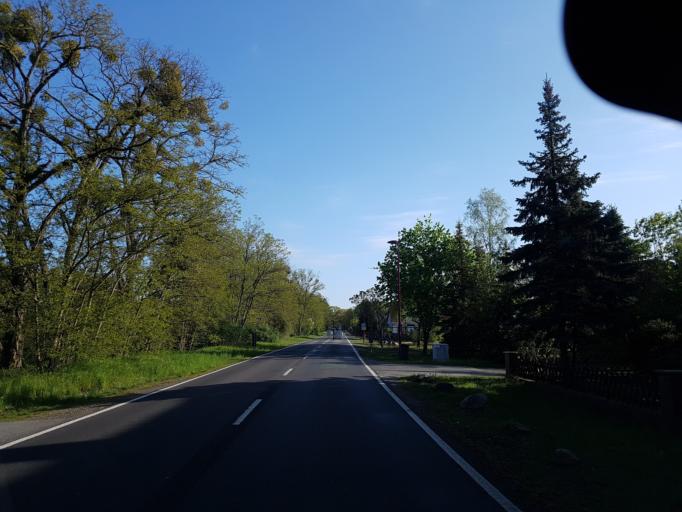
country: DE
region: Brandenburg
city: Grossraschen
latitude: 51.5989
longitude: 14.0155
